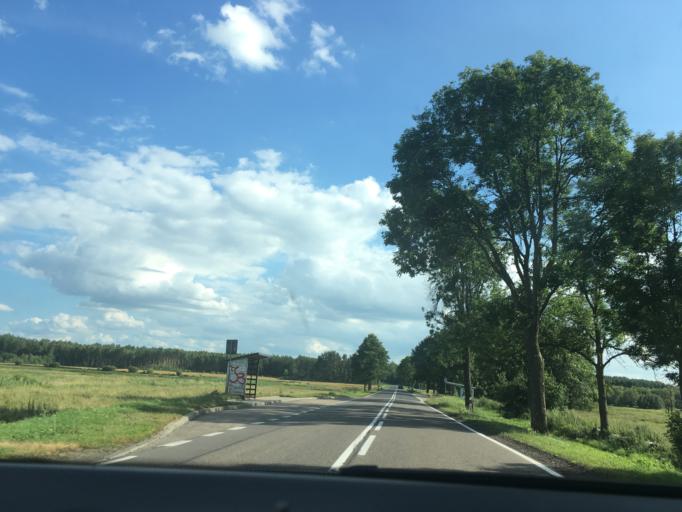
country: PL
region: Podlasie
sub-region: Powiat bielski
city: Bielsk Podlaski
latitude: 52.8774
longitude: 23.2040
